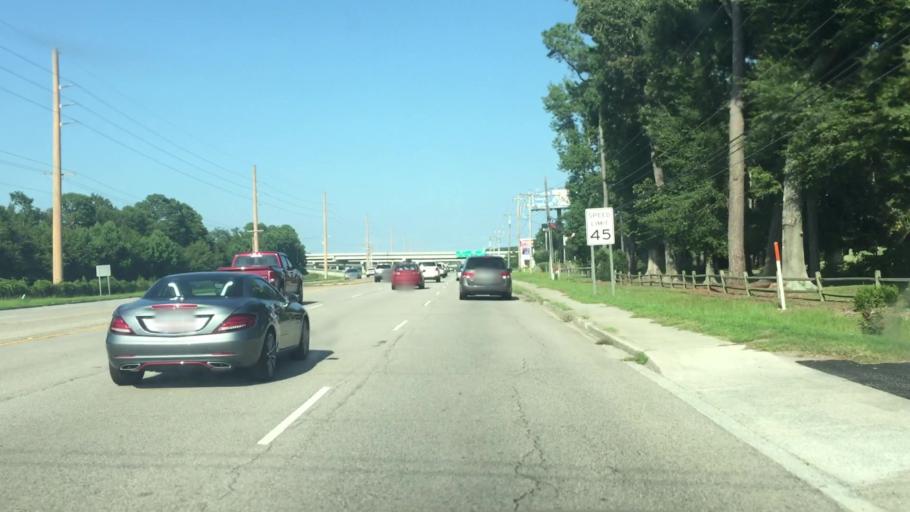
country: US
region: South Carolina
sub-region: Horry County
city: North Myrtle Beach
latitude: 33.7851
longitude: -78.7813
